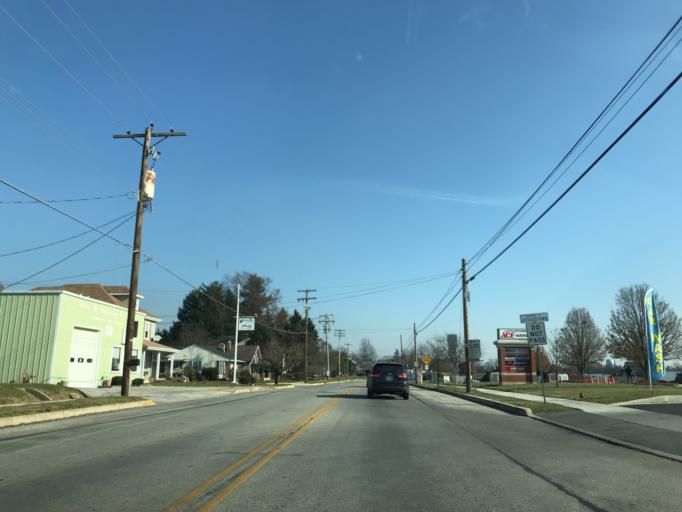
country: US
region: Pennsylvania
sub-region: Adams County
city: Littlestown
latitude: 39.7426
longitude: -77.1020
